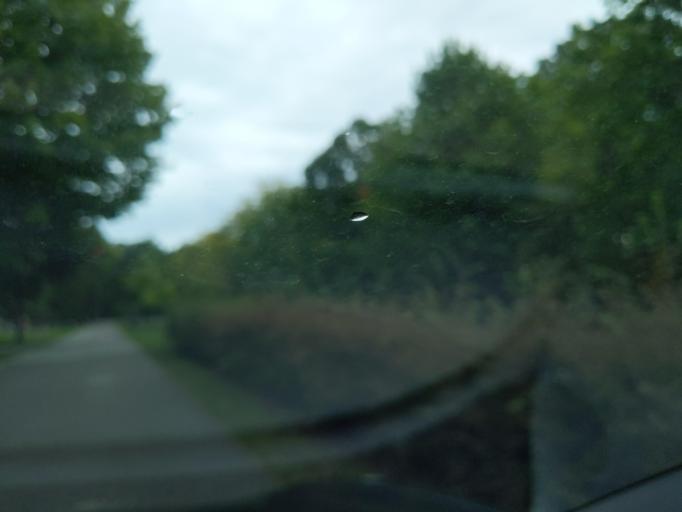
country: US
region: Michigan
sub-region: Grand Traverse County
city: Traverse City
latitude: 44.7563
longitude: -85.5873
